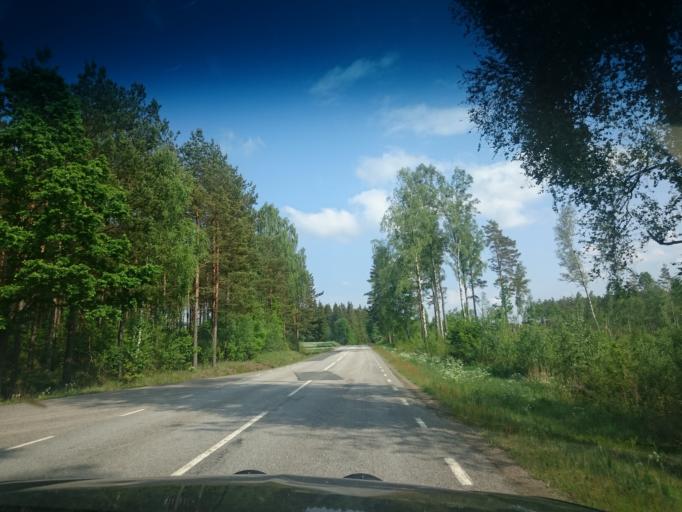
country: SE
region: Joenkoeping
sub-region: Vetlanda Kommun
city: Vetlanda
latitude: 57.3802
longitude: 15.0319
